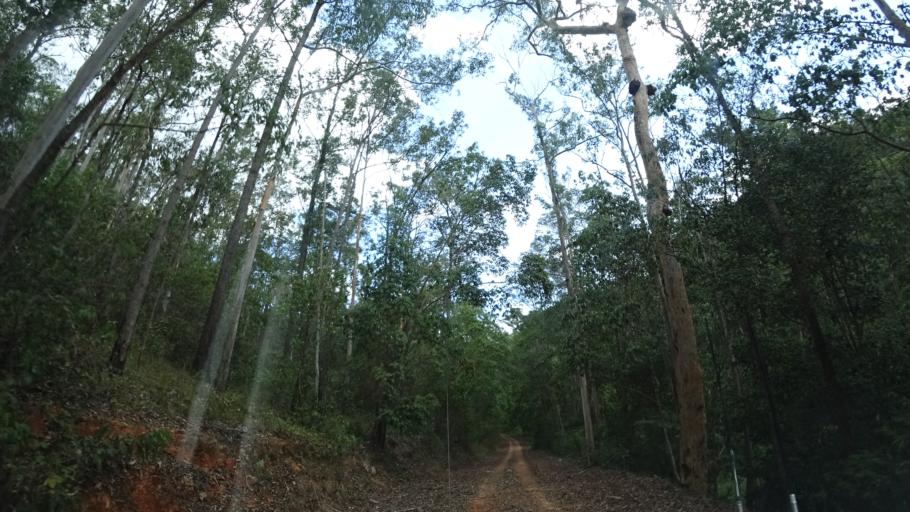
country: AU
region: Queensland
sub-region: Moreton Bay
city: Highvale
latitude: -27.3473
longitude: 152.7297
